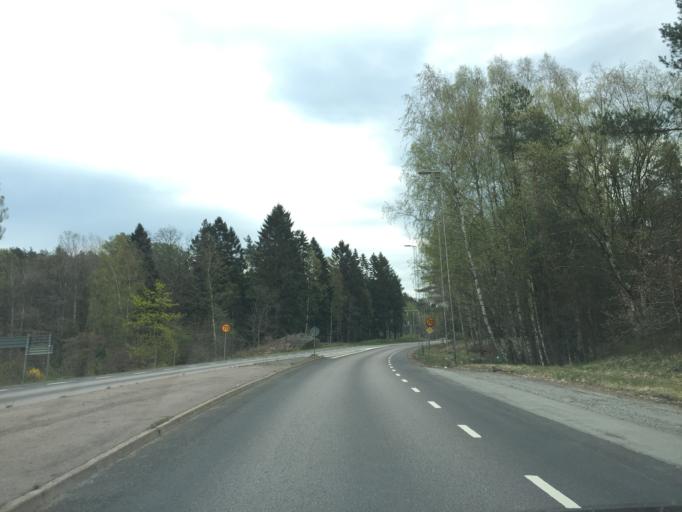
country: SE
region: Vaestra Goetaland
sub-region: Goteborg
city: Loevgaerdet
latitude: 57.8088
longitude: 12.0528
